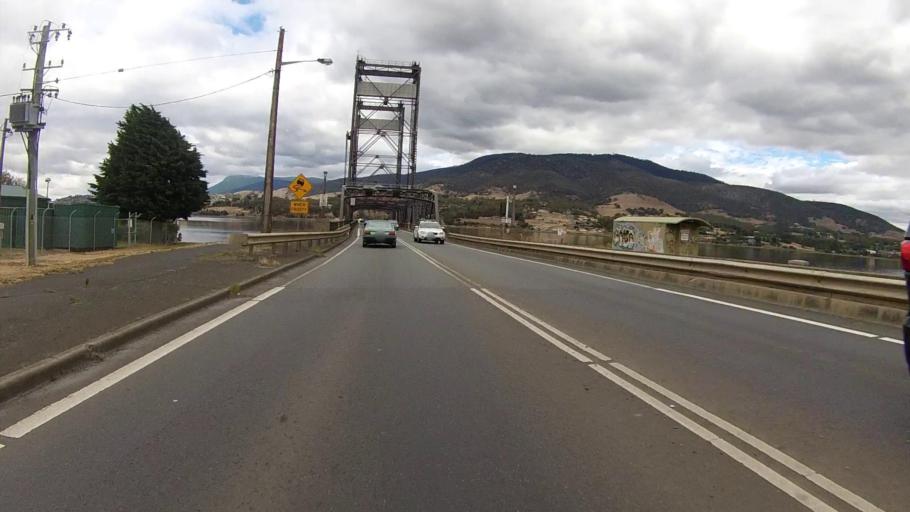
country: AU
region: Tasmania
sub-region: Brighton
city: Bridgewater
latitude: -42.7393
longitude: 147.2267
